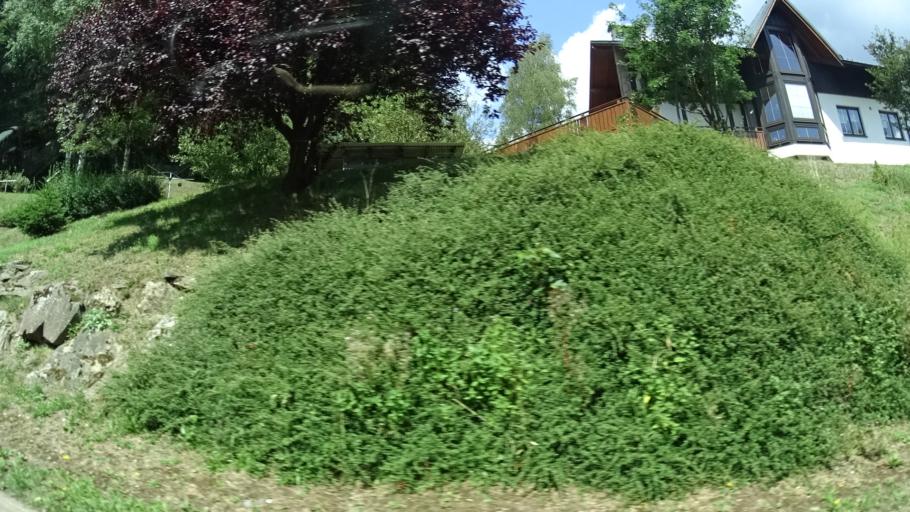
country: DE
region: Thuringia
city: Altenfeld
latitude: 50.5657
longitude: 10.9748
